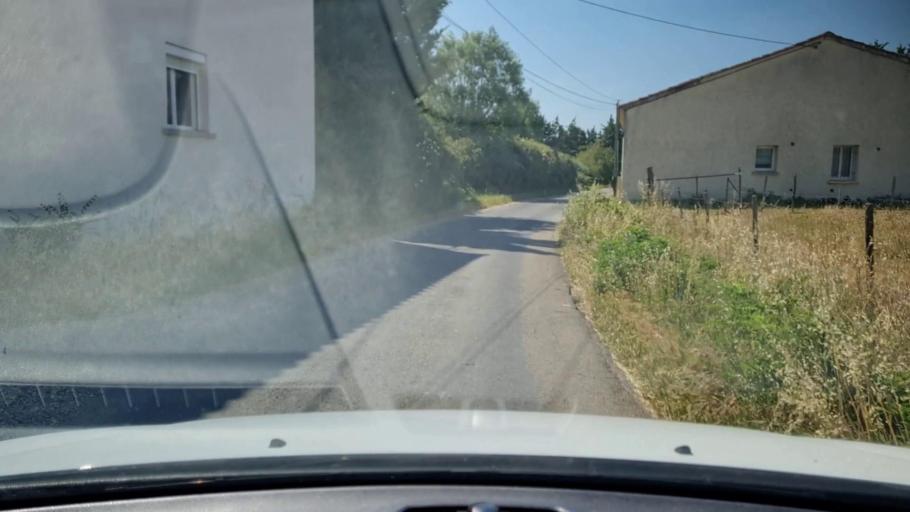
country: FR
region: Languedoc-Roussillon
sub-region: Departement du Gard
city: Le Cailar
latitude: 43.6612
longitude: 4.2336
